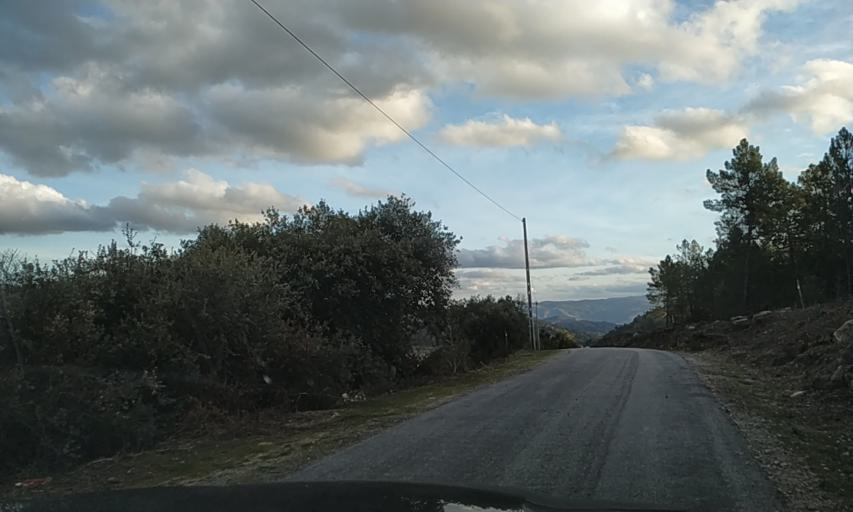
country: PT
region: Braganca
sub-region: Carrazeda de Ansiaes
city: Carrazeda de Anciaes
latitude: 41.2130
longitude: -7.3635
